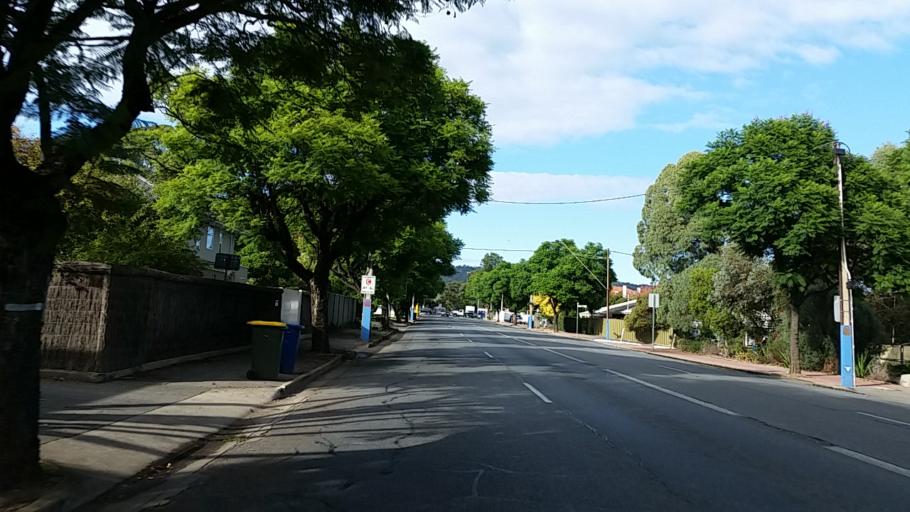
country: AU
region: South Australia
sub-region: Unley
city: Fullarton
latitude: -34.9628
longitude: 138.6264
